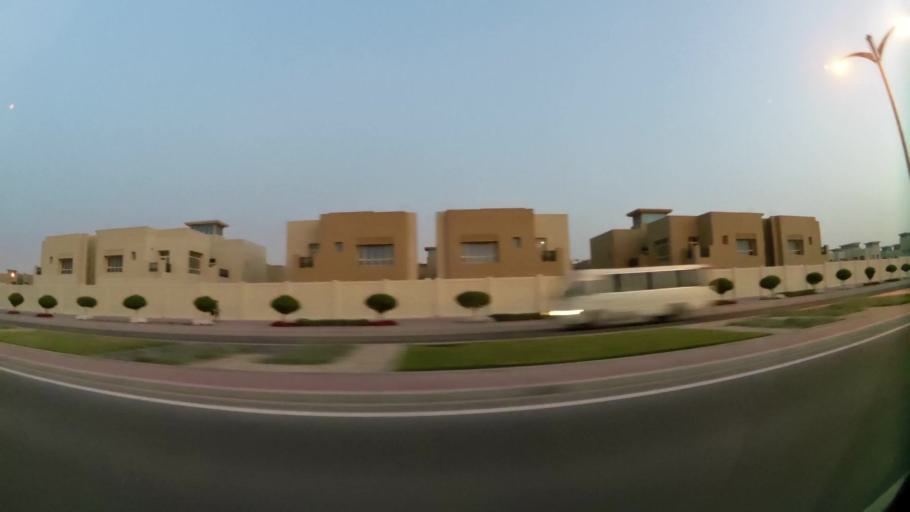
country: QA
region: Baladiyat ad Dawhah
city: Doha
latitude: 25.2629
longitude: 51.4714
